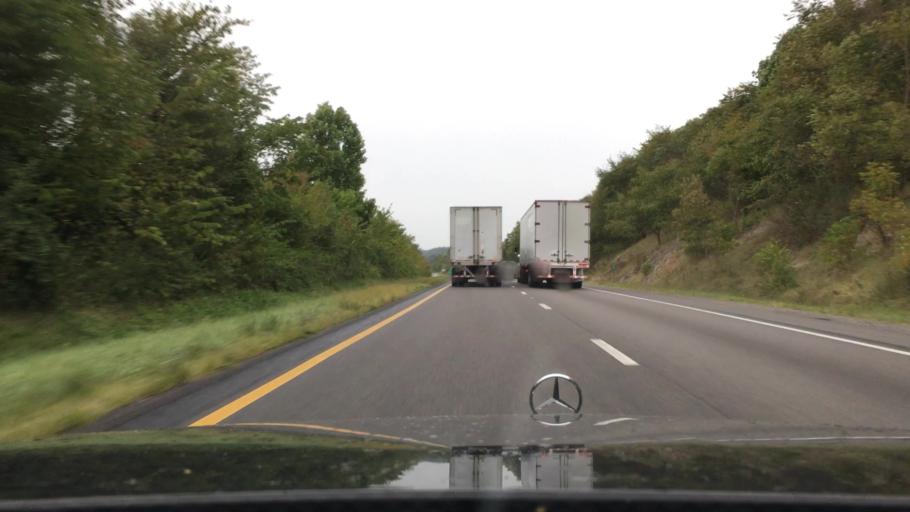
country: US
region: Virginia
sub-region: Smyth County
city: Atkins
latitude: 36.8946
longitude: -81.3562
